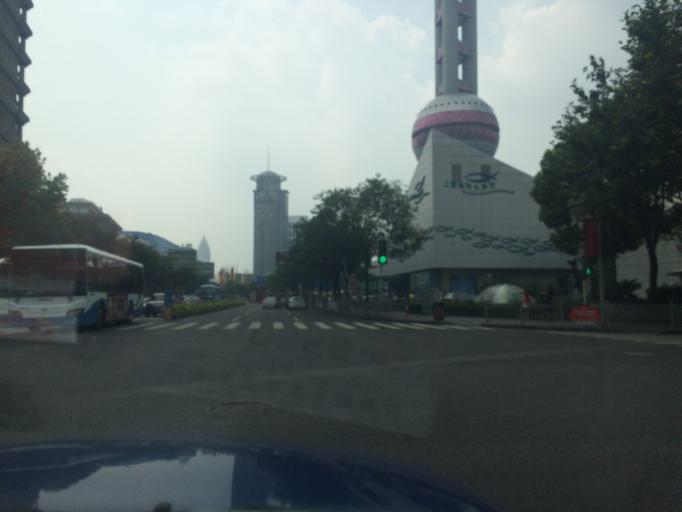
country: CN
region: Shanghai Shi
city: Hongkou
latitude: 31.2431
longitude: 121.4987
